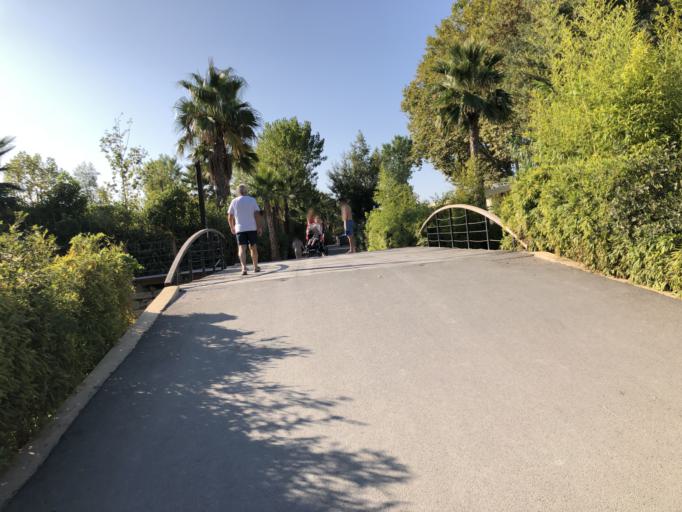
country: FR
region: Provence-Alpes-Cote d'Azur
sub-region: Departement du Var
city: Gassin
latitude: 43.2787
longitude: 6.5810
